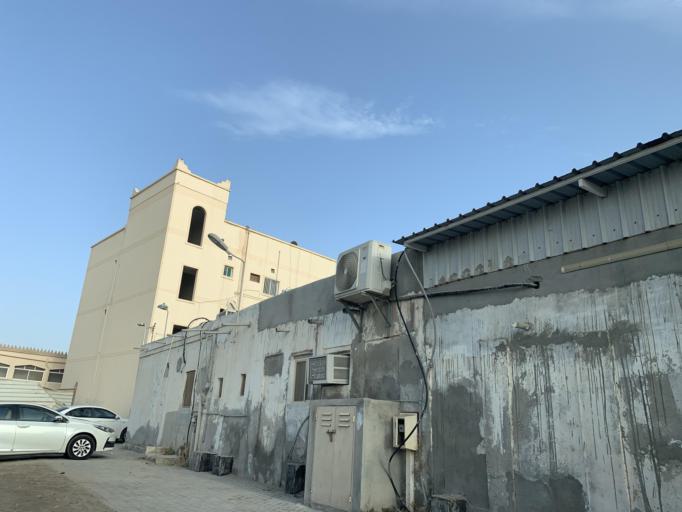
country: BH
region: Manama
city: Manama
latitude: 26.1805
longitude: 50.5830
